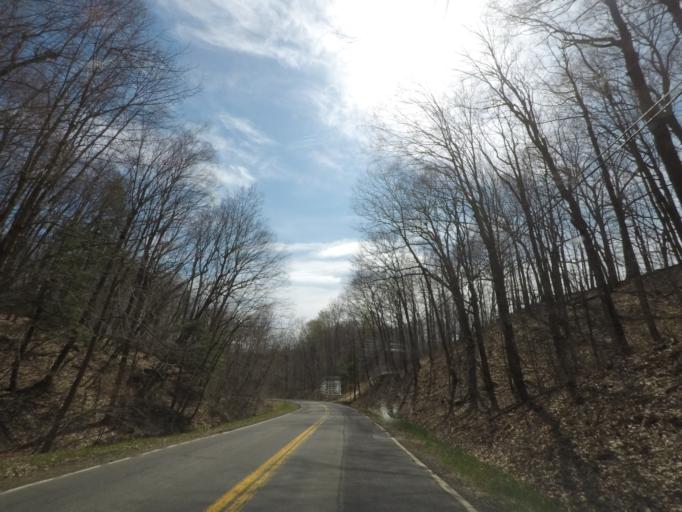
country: US
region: New York
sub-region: Columbia County
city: Chatham
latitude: 42.3679
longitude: -73.5311
